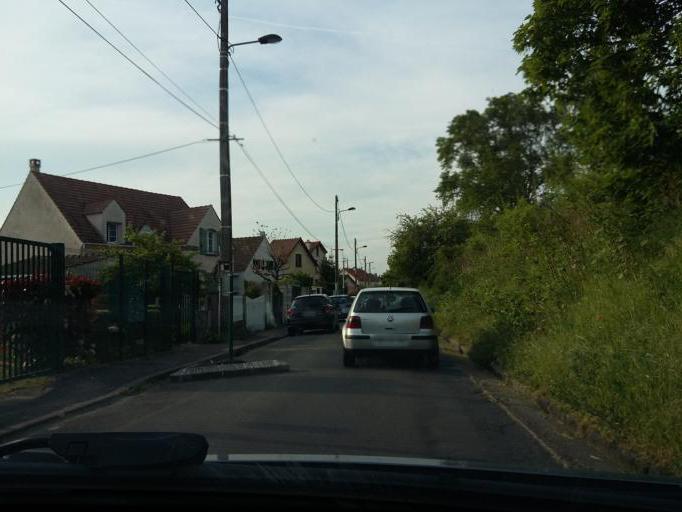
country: FR
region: Ile-de-France
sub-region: Departement du Val-d'Oise
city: Ermont
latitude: 48.9754
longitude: 2.2627
